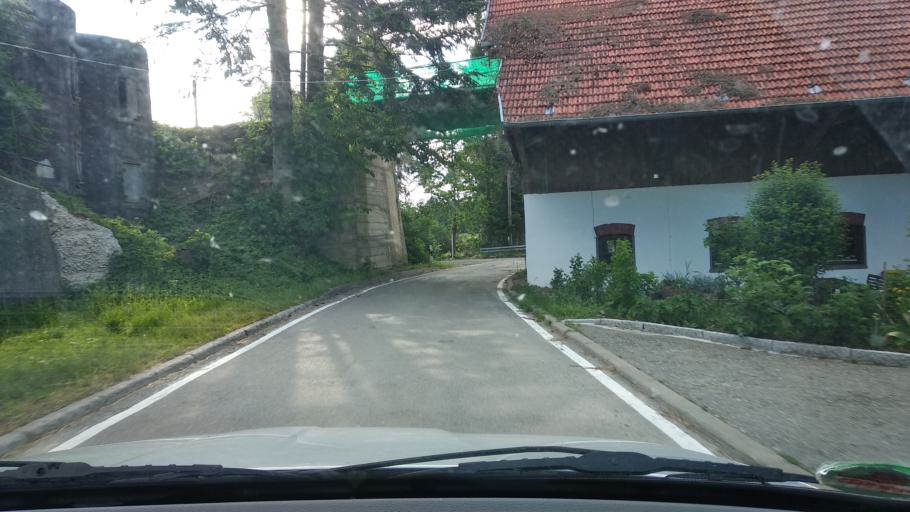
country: DE
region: Baden-Wuerttemberg
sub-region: Tuebingen Region
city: Aitrach
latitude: 47.9605
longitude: 10.0415
